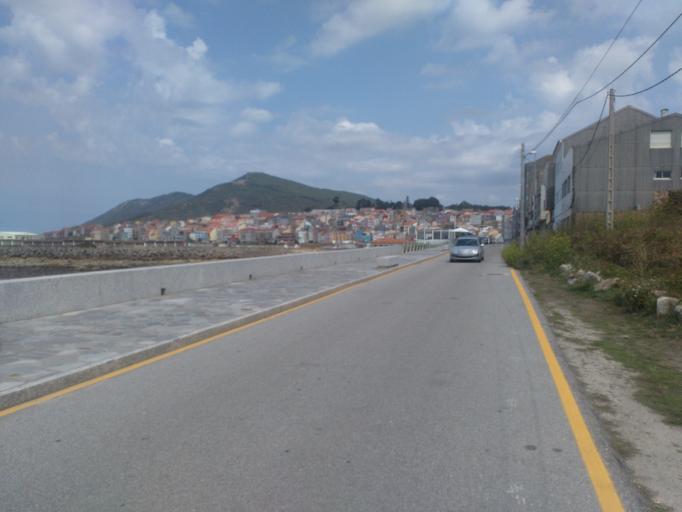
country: ES
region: Galicia
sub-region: Provincia de Pontevedra
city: A Guarda
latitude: 41.8956
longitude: -8.8779
